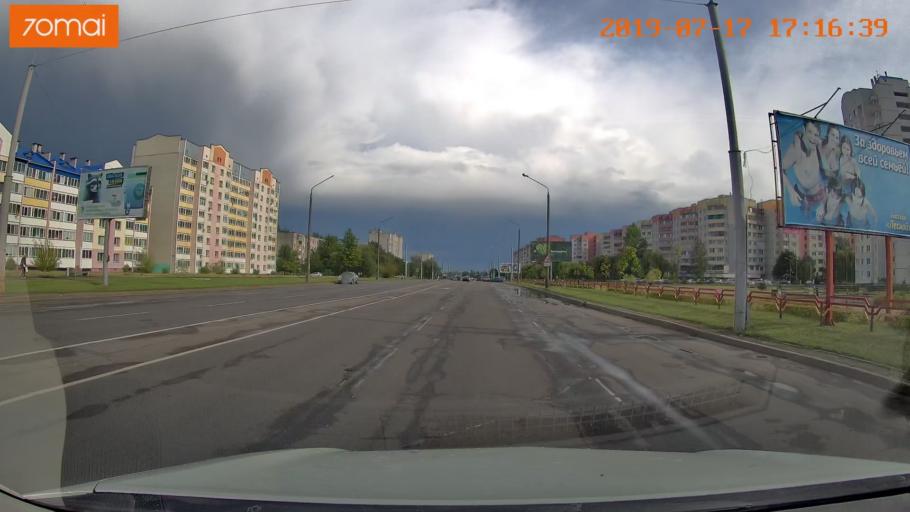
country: BY
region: Mogilev
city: Babruysk
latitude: 53.1663
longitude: 29.1945
